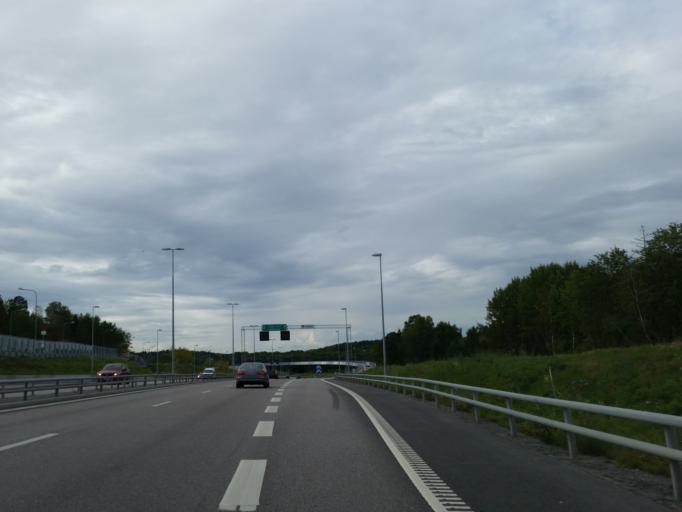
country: SE
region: Stockholm
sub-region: Stockholms Kommun
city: Kista
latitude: 59.3956
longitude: 17.9168
